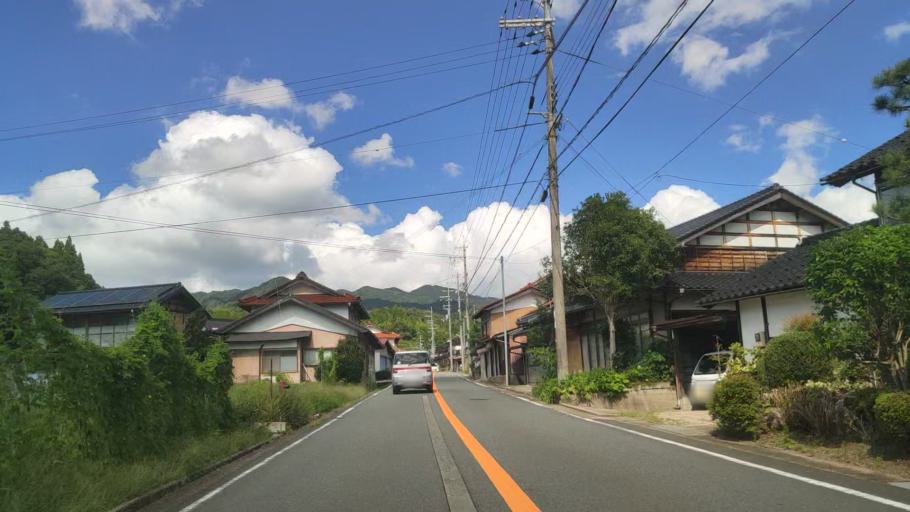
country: JP
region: Hyogo
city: Toyooka
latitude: 35.4878
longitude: 134.9529
